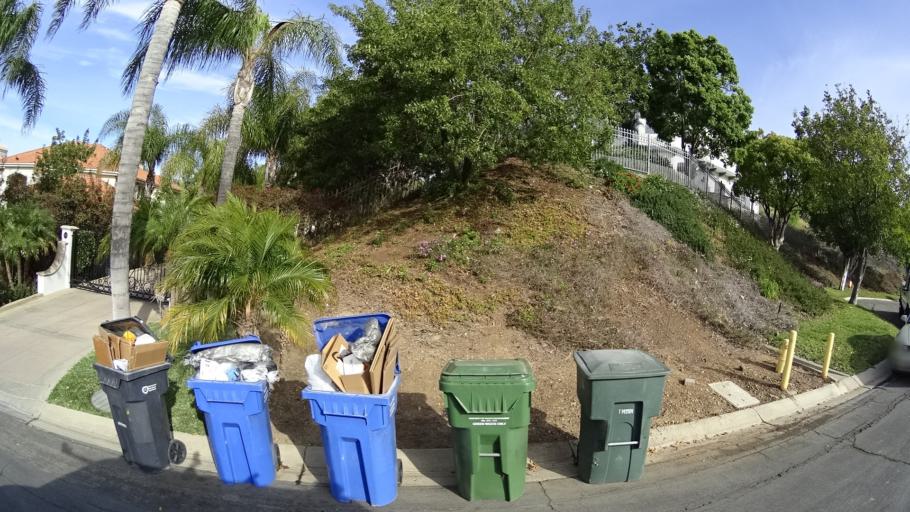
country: US
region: California
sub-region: Ventura County
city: Oak Park
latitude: 34.1890
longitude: -118.7896
